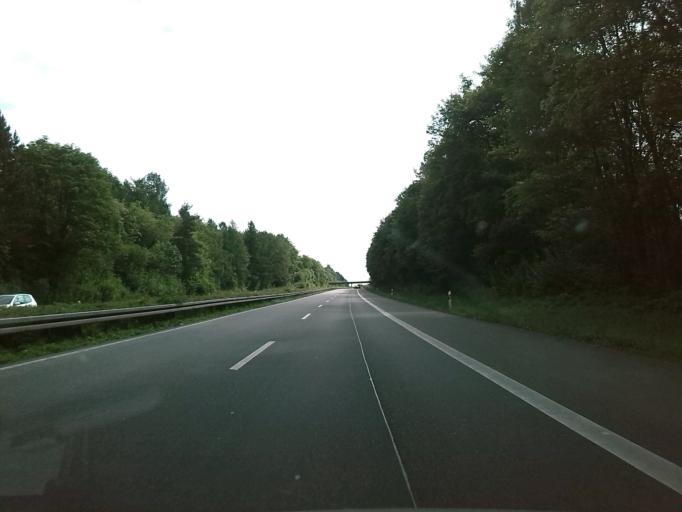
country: DE
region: Hesse
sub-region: Regierungsbezirk Darmstadt
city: Rossdorf
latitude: 49.8688
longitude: 8.7360
